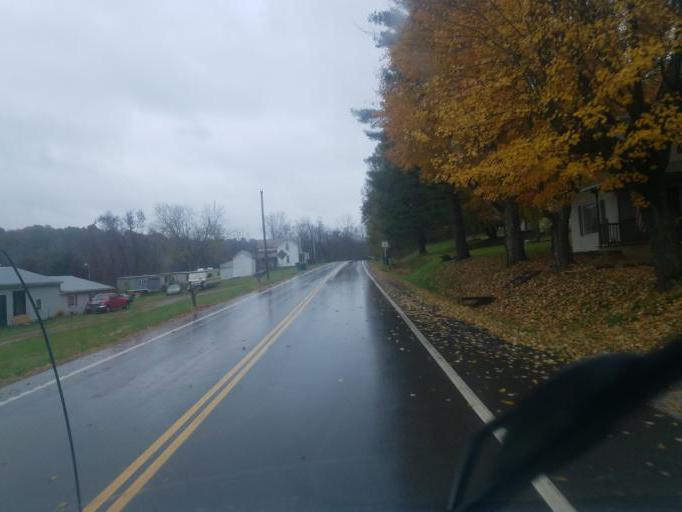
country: US
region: Ohio
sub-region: Muskingum County
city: Frazeysburg
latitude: 40.2020
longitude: -82.2351
